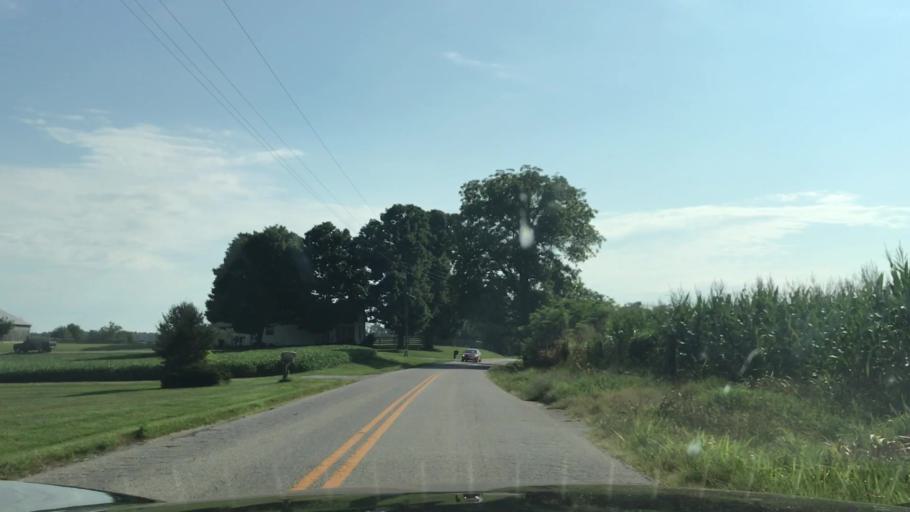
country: US
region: Kentucky
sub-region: Hart County
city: Horse Cave
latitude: 37.1865
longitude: -85.7697
